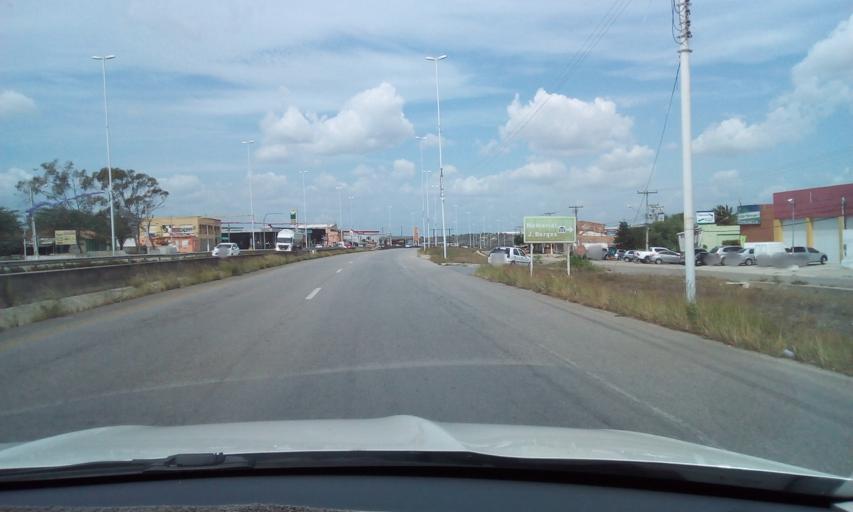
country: BR
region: Pernambuco
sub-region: Bezerros
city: Bezerros
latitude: -8.2396
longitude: -35.7475
